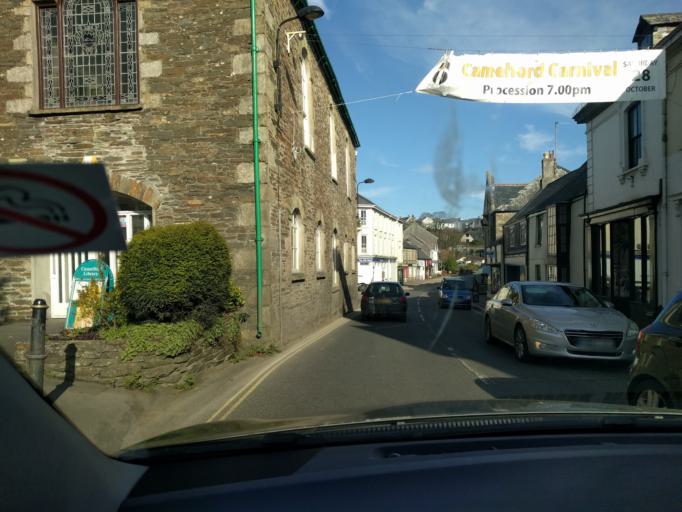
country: GB
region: England
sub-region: Cornwall
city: Camelford
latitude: 50.6224
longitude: -4.6794
